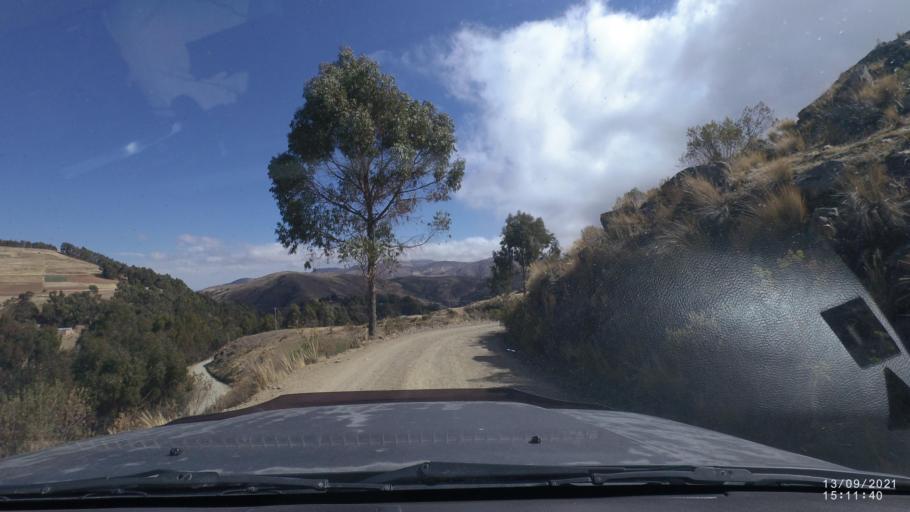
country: BO
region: Cochabamba
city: Colomi
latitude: -17.3605
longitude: -65.8043
